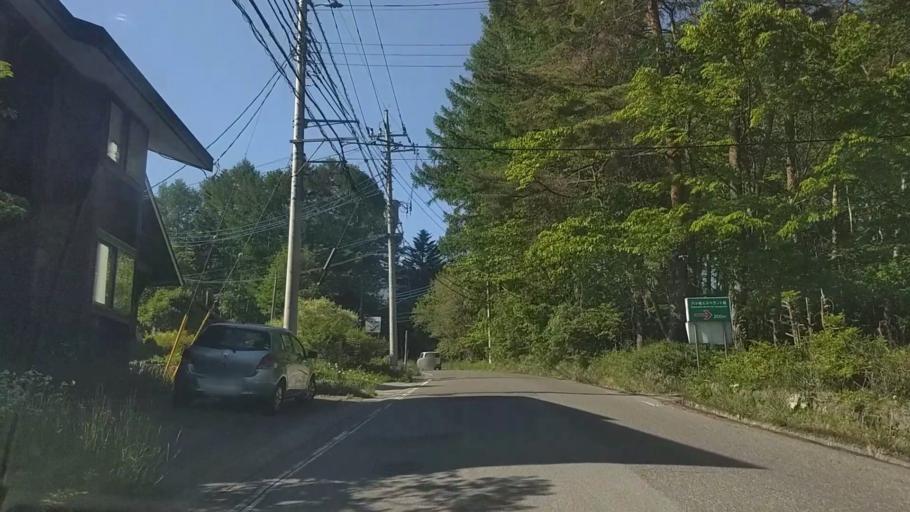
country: JP
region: Yamanashi
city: Nirasaki
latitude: 35.8805
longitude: 138.3565
